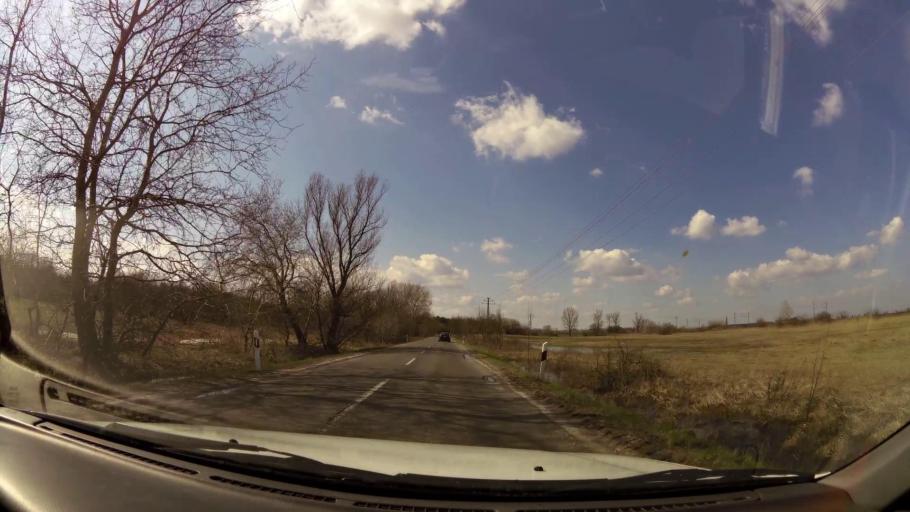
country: HU
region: Pest
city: Farmos
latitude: 47.3575
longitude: 19.8223
